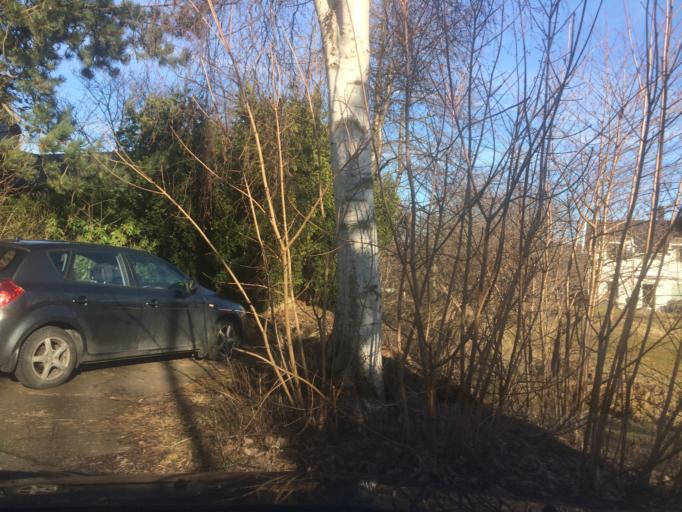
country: SE
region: Vaestra Goetaland
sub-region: Goteborg
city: Goeteborg
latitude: 57.7526
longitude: 11.9348
